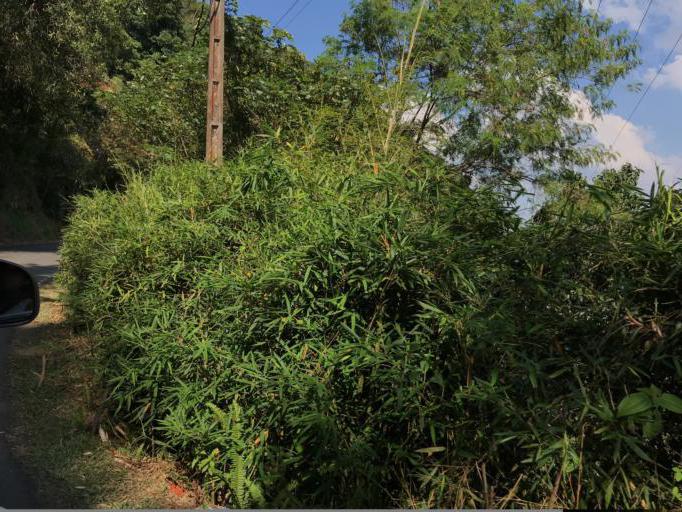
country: CO
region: Valle del Cauca
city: Cali
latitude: 3.4805
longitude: -76.6128
